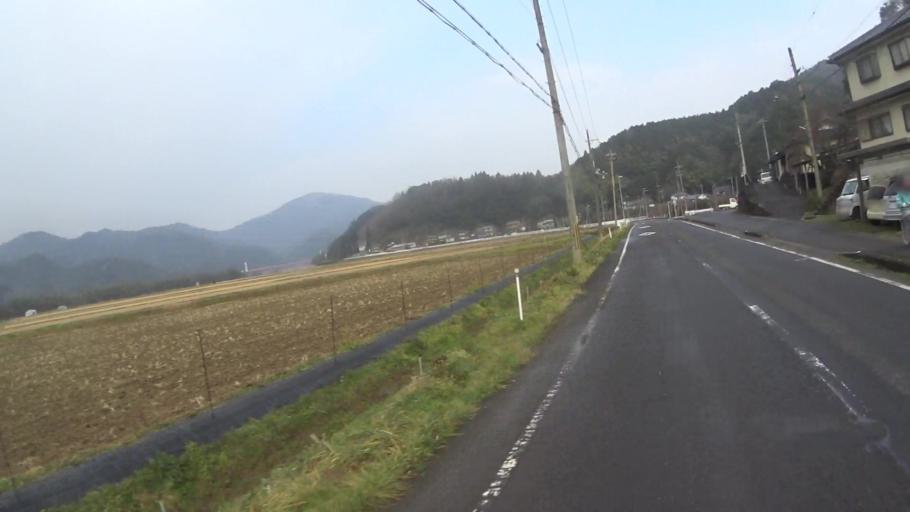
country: JP
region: Kyoto
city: Maizuru
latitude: 35.4598
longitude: 135.2874
